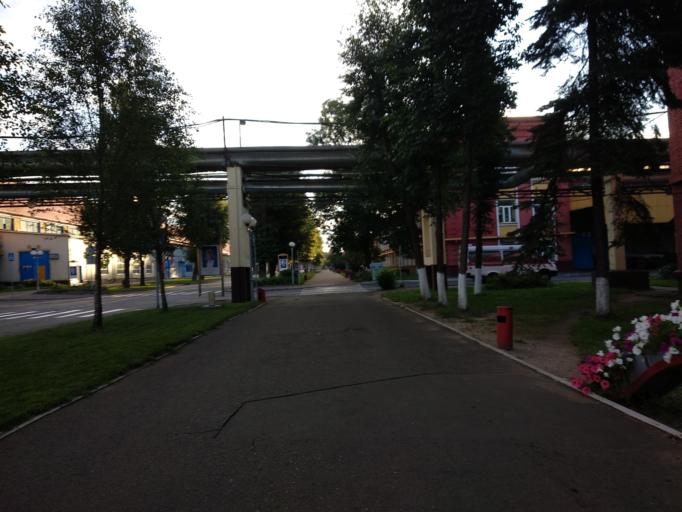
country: BY
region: Minsk
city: Minsk
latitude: 53.8917
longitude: 27.6212
